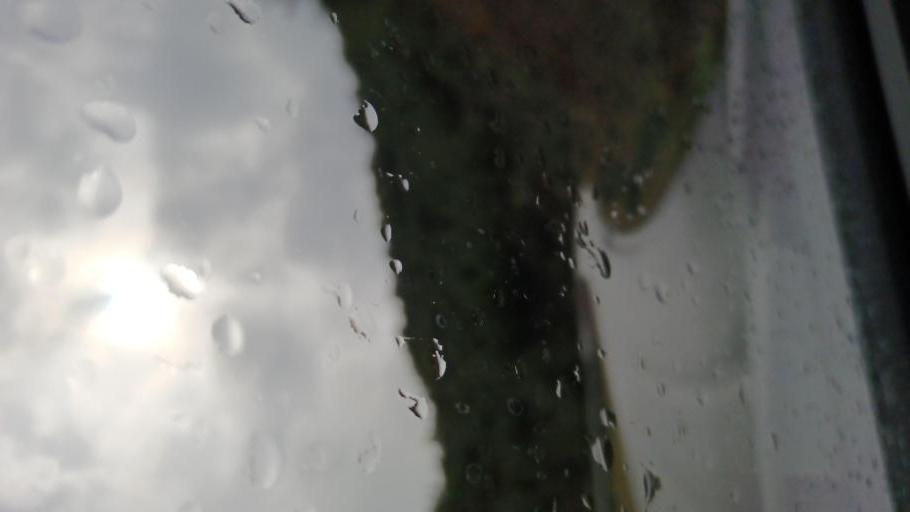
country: CY
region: Lefkosia
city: Kato Pyrgos
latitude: 35.1064
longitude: 32.7508
